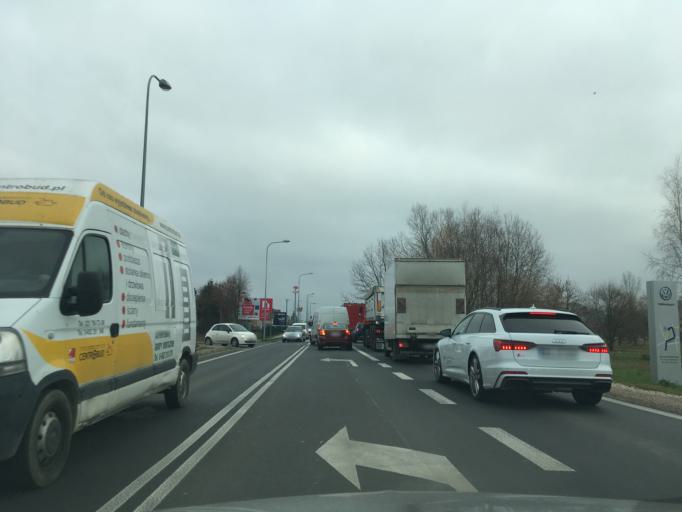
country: PL
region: Masovian Voivodeship
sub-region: Powiat piaseczynski
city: Piaseczno
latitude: 52.0821
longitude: 21.0106
